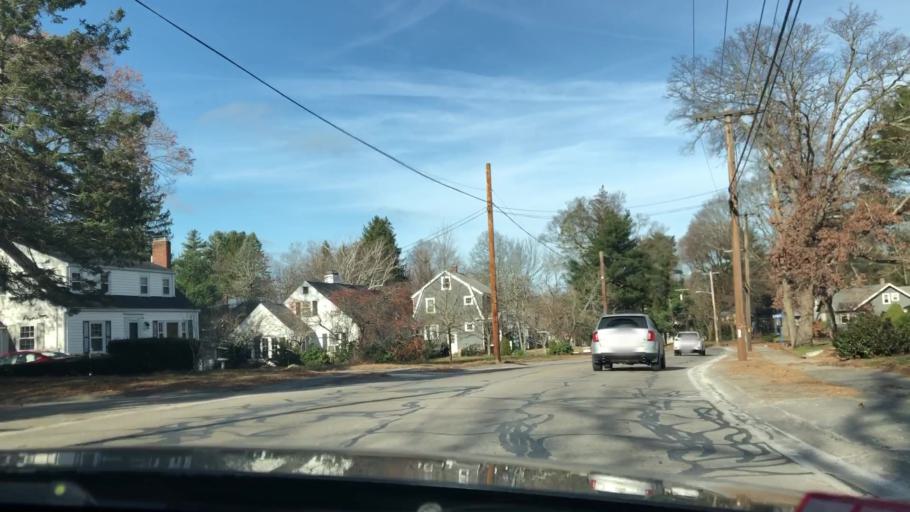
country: US
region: Massachusetts
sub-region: Norfolk County
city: Walpole
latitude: 42.1317
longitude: -71.2437
